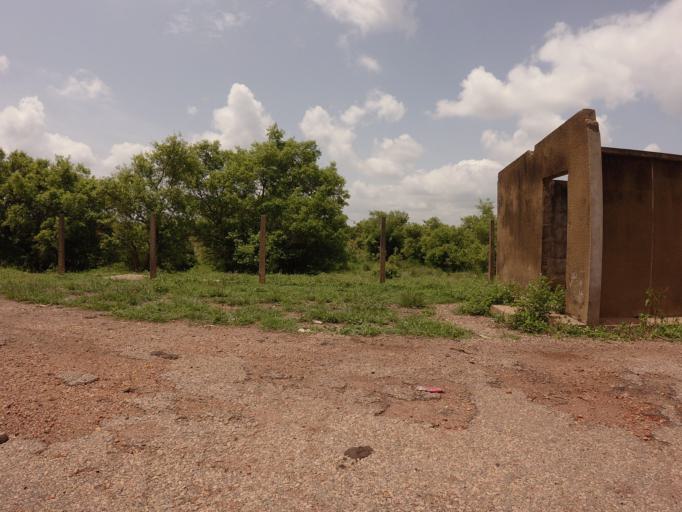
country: GH
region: Northern
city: Tamale
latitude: 9.1412
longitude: -1.1583
